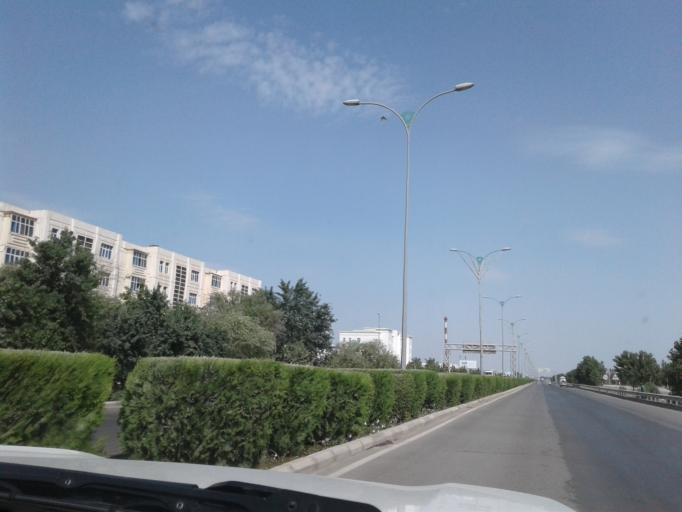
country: TM
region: Dasoguz
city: Dasoguz
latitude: 41.8358
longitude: 59.9285
